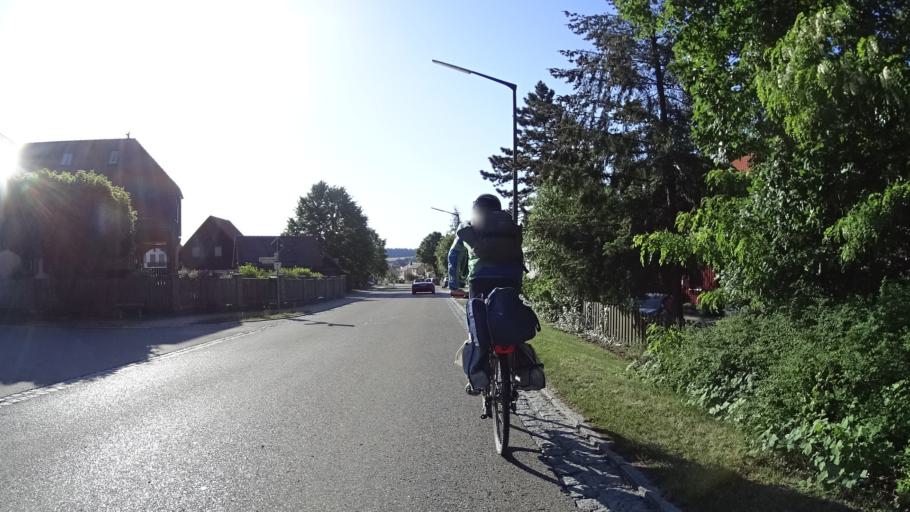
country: DE
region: Bavaria
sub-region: Regierungsbezirk Mittelfranken
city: Dentlein am Forst
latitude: 49.1491
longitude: 10.4142
